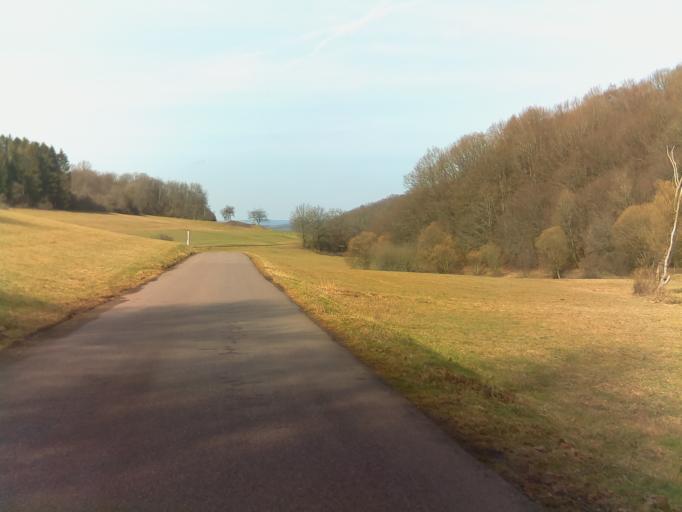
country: DE
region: Rheinland-Pfalz
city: Hahnweiler
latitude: 49.5389
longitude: 7.2064
